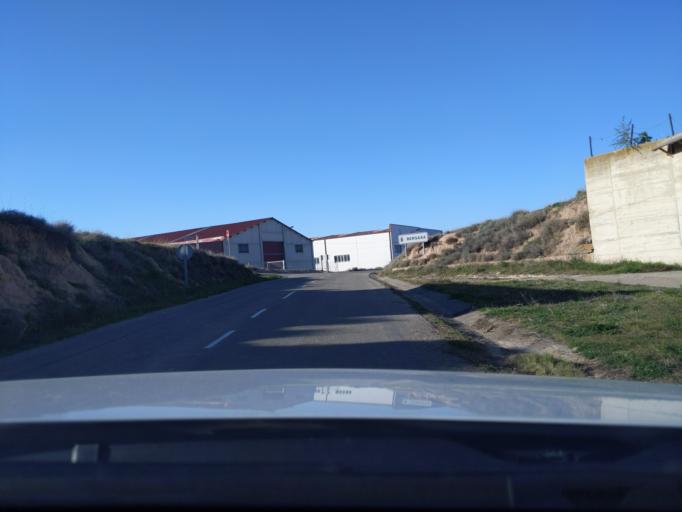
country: ES
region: La Rioja
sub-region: Provincia de La Rioja
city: Bergasa
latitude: 42.2513
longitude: -2.1350
